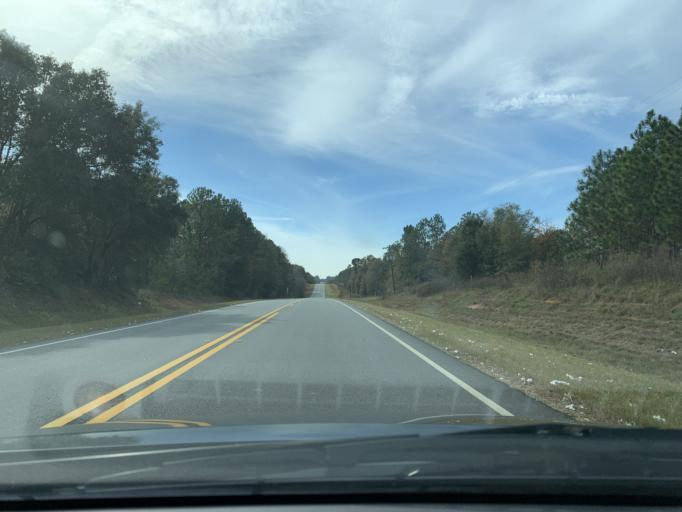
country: US
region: Georgia
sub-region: Turner County
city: Ashburn
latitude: 31.7597
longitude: -83.5457
